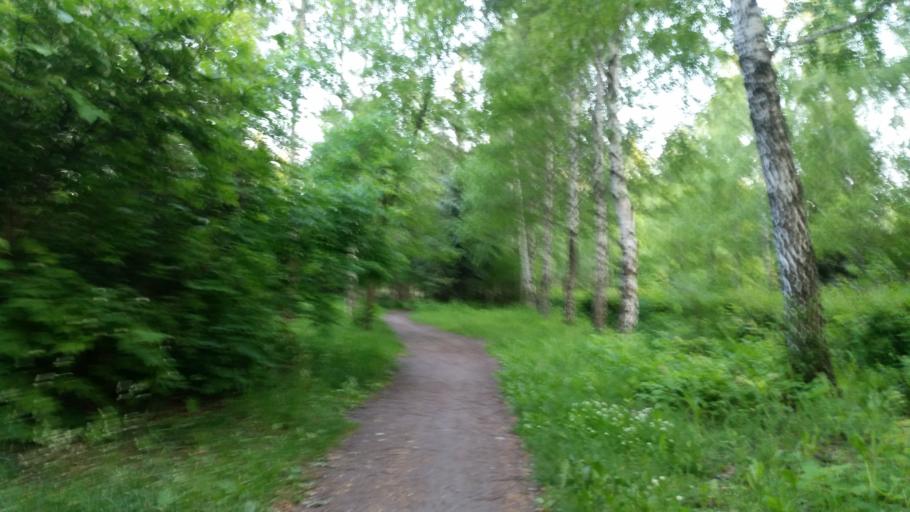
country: RU
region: Ulyanovsk
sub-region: Ulyanovskiy Rayon
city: Ulyanovsk
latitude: 54.3482
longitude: 48.3941
